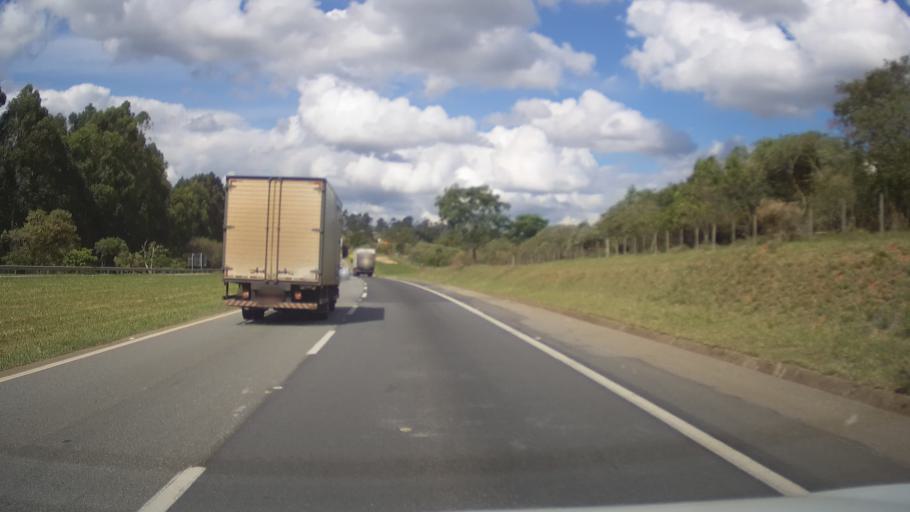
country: BR
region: Minas Gerais
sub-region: Oliveira
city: Oliveira
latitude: -20.8286
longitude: -44.8082
